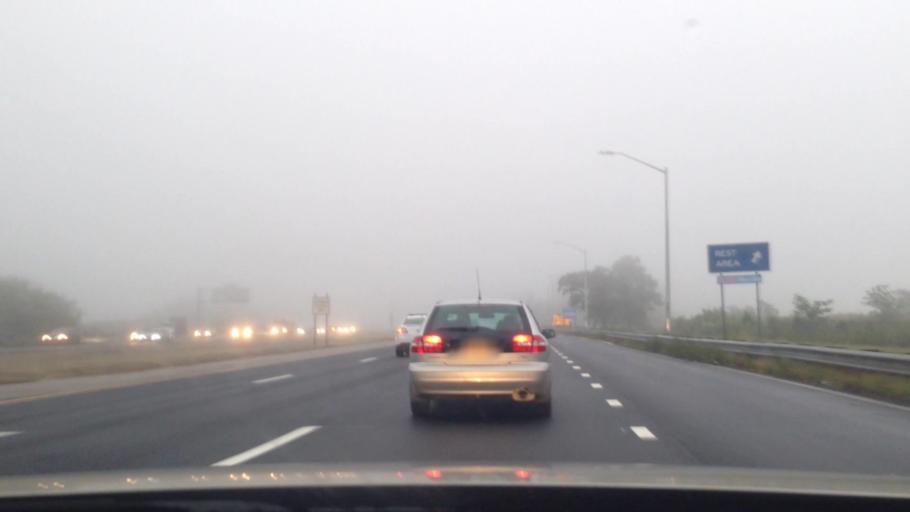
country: US
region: New York
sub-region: Kings County
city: Coney Island
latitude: 40.5836
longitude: -73.9239
